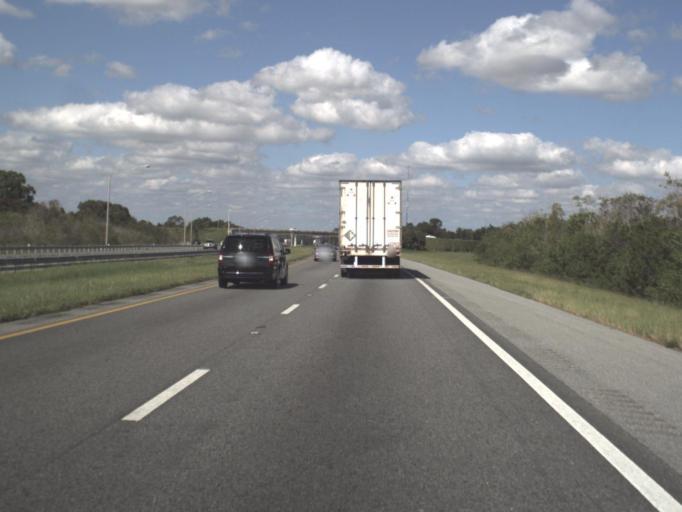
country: US
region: Florida
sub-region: Osceola County
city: Buenaventura Lakes
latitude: 28.2870
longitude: -81.3434
